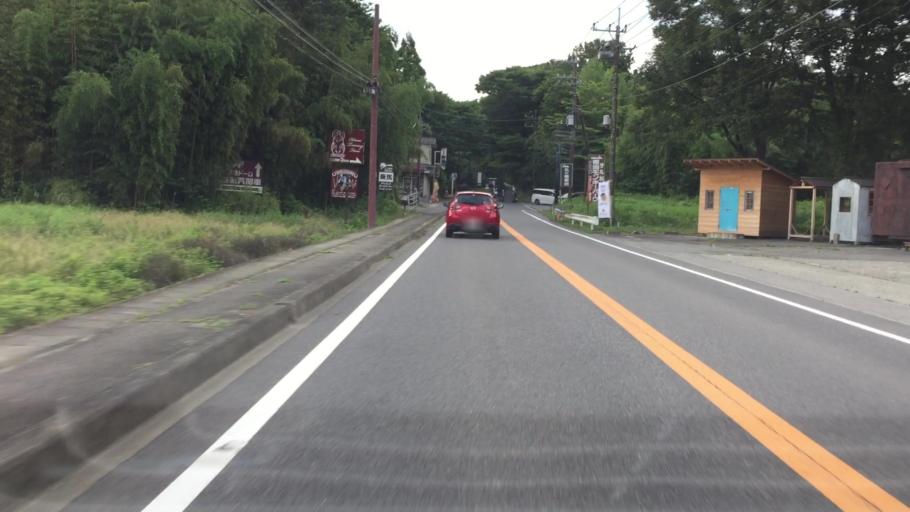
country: JP
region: Tochigi
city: Kuroiso
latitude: 37.0104
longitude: 140.0310
